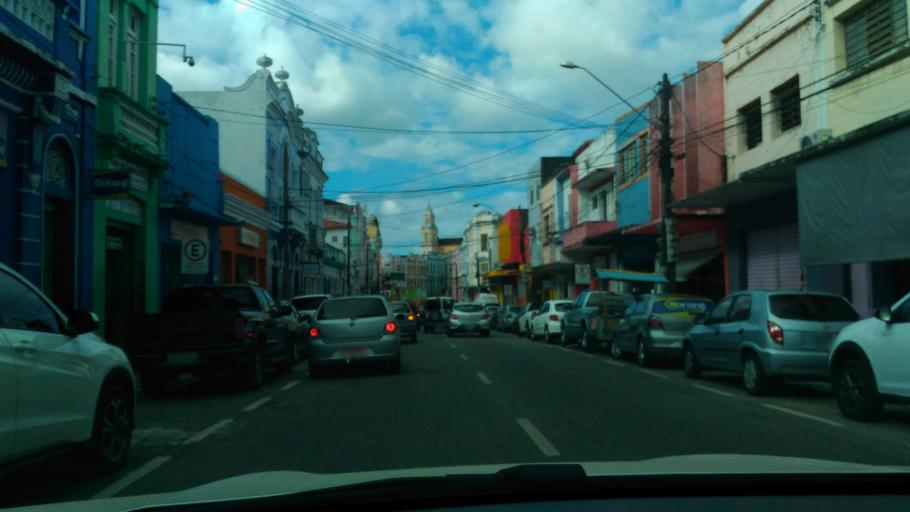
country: BR
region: Paraiba
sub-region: Joao Pessoa
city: Joao Pessoa
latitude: -7.1154
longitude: -34.8888
